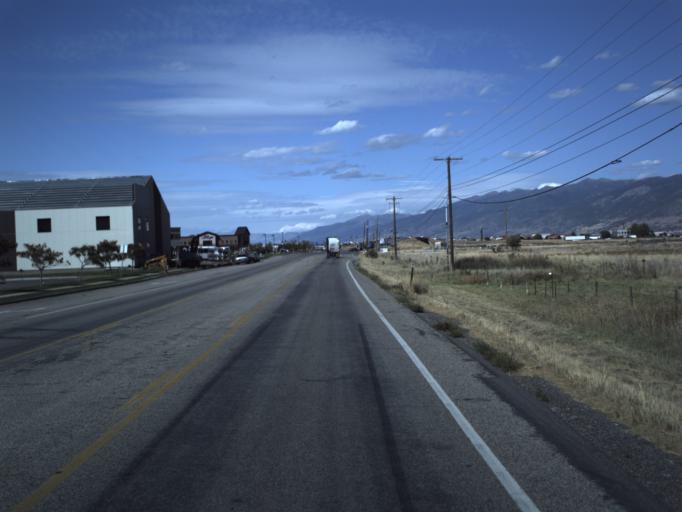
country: US
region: Utah
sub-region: Davis County
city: North Salt Lake
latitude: 40.8277
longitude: -111.9373
